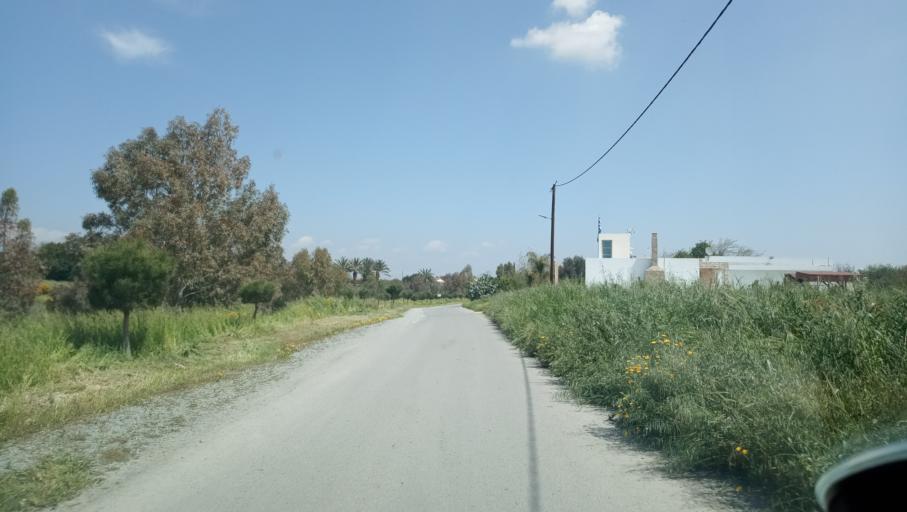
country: CY
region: Lefkosia
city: Dali
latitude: 35.0227
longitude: 33.4089
